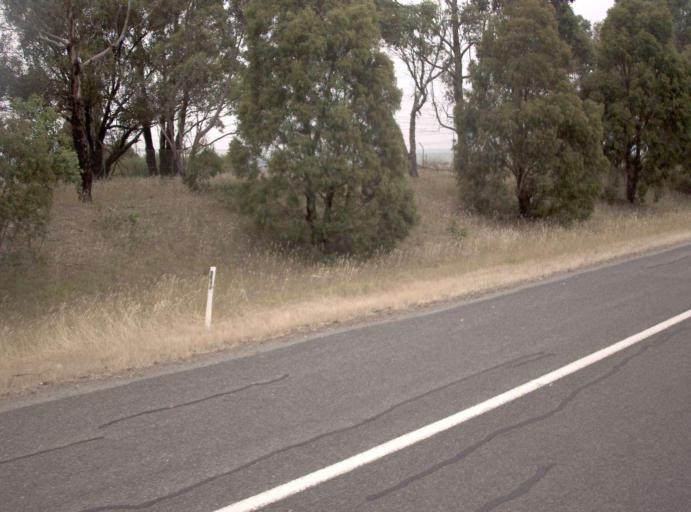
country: AU
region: Victoria
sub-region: Latrobe
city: Morwell
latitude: -38.2438
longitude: 146.4007
